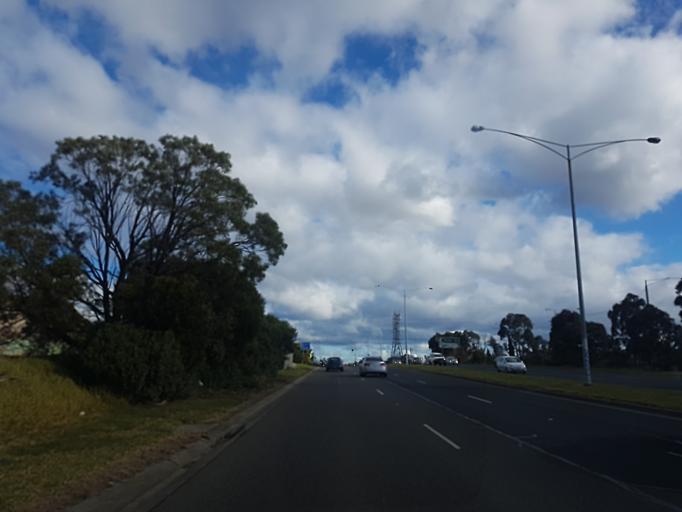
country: AU
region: Victoria
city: Watsonia
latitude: -37.7092
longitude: 145.0866
